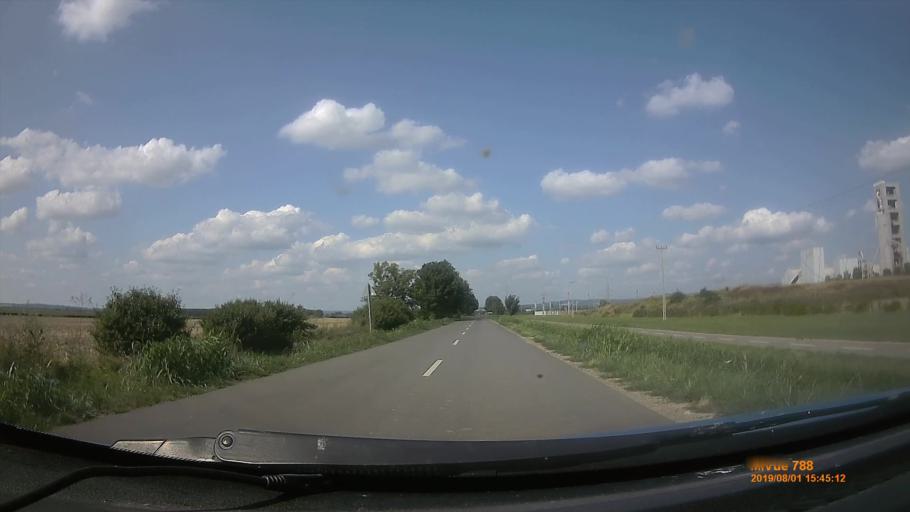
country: HU
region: Baranya
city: Szentlorinc
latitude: 46.0137
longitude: 17.9758
